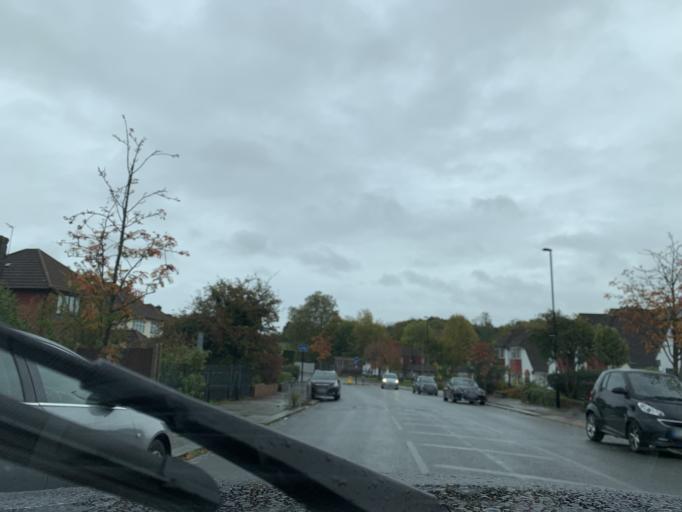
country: GB
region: England
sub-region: Greater London
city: Blackheath
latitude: 51.4416
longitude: 0.0270
